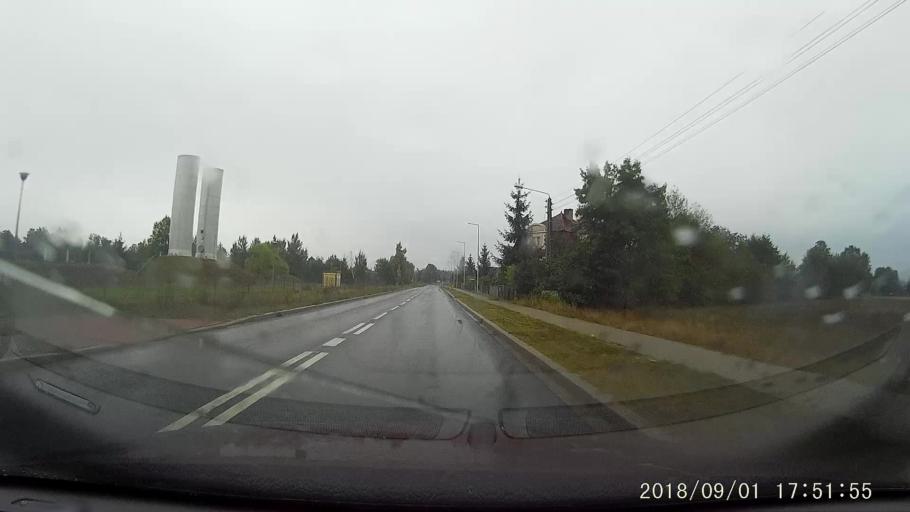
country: PL
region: Lubusz
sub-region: Powiat zaganski
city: Ilowa
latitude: 51.4935
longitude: 15.1927
